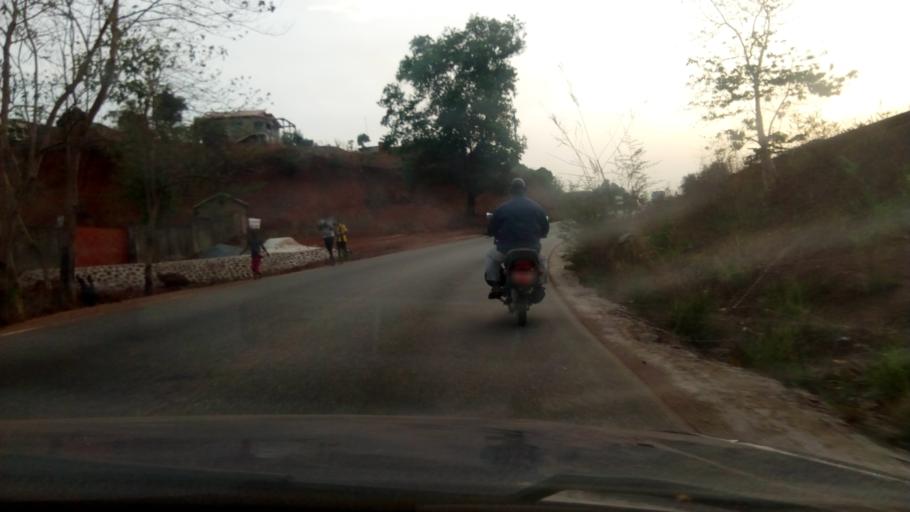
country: GN
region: Kindia
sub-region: Prefecture de Dubreka
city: Dubreka
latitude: 9.7426
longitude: -13.5034
